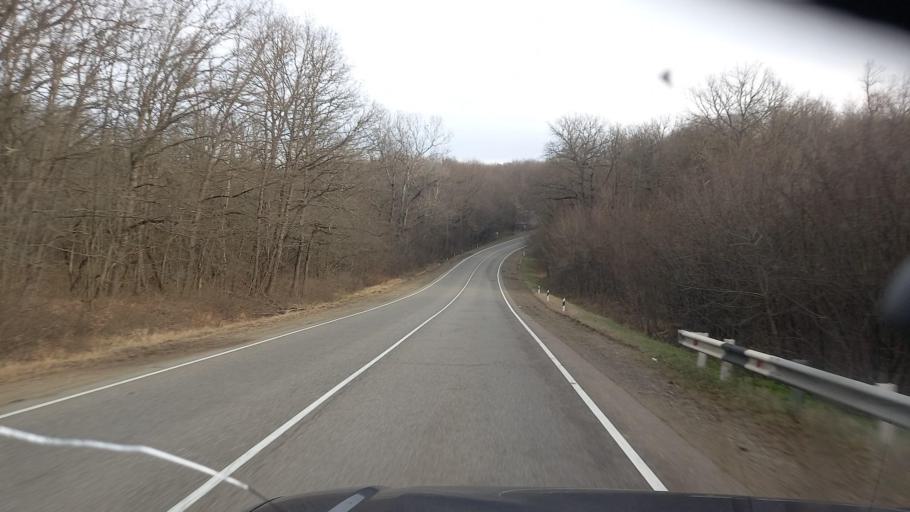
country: RU
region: Adygeya
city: Ponezhukay
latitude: 44.6658
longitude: 39.4709
